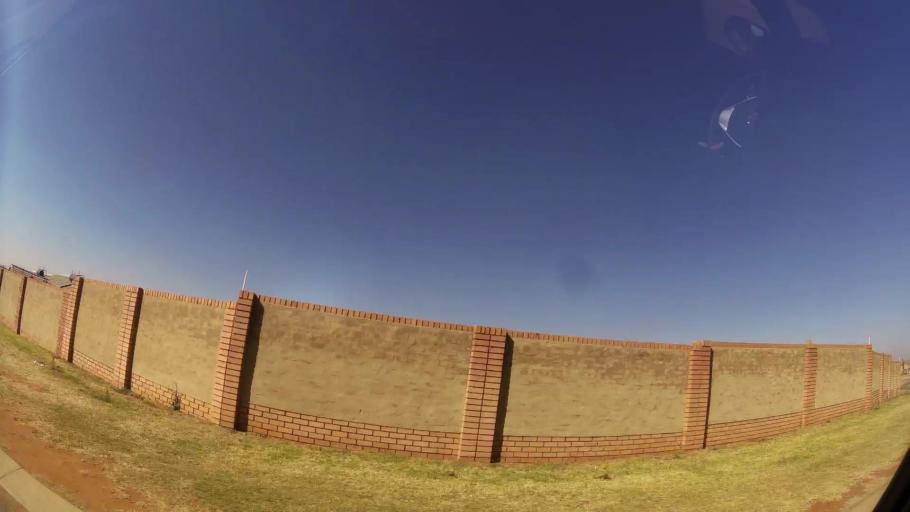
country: ZA
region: Gauteng
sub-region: City of Johannesburg Metropolitan Municipality
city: Midrand
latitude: -25.9488
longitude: 28.1028
